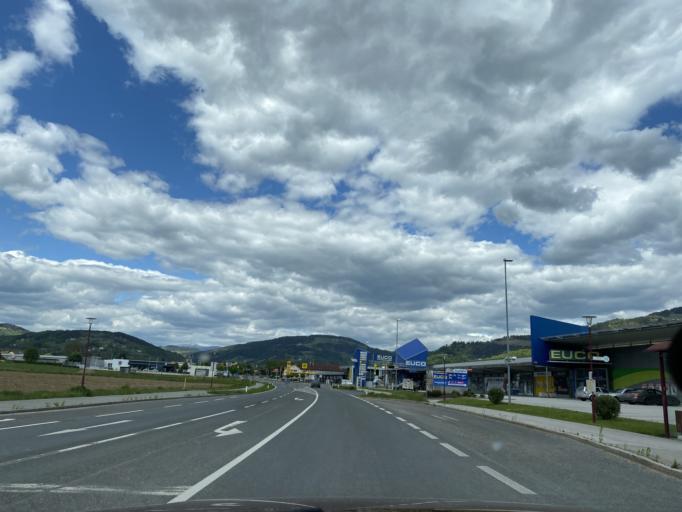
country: AT
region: Carinthia
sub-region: Politischer Bezirk Wolfsberg
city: Wolfsberg
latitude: 46.8242
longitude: 14.8393
